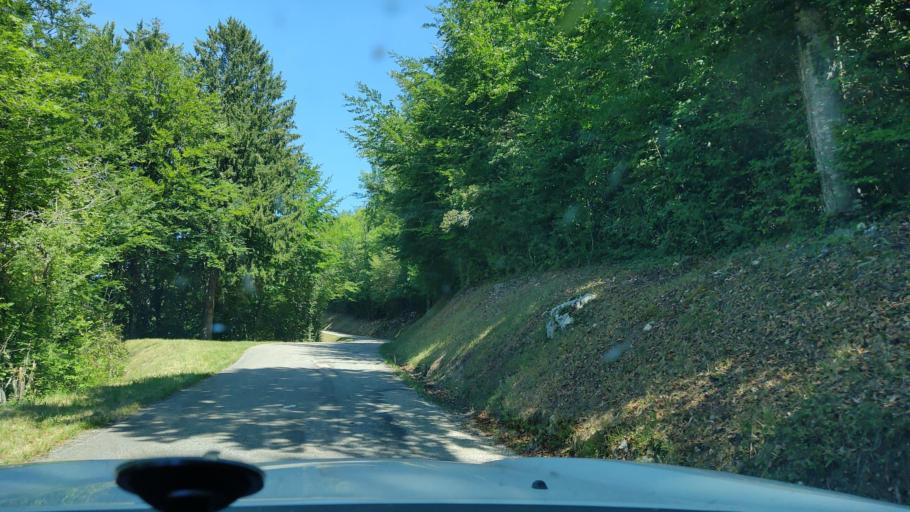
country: FR
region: Rhone-Alpes
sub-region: Departement de la Savoie
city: Le Bourget-du-Lac
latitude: 45.6497
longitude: 5.8002
